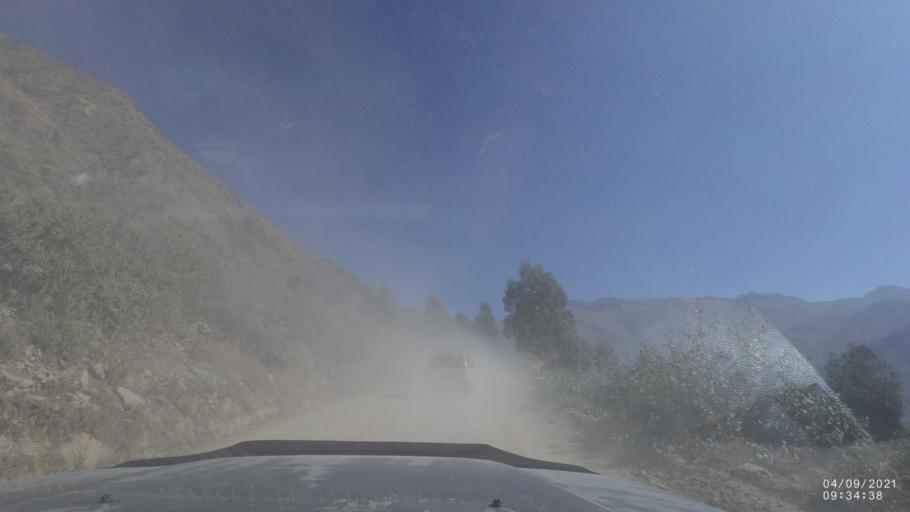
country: BO
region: Cochabamba
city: Sipe Sipe
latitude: -17.3564
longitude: -66.3793
